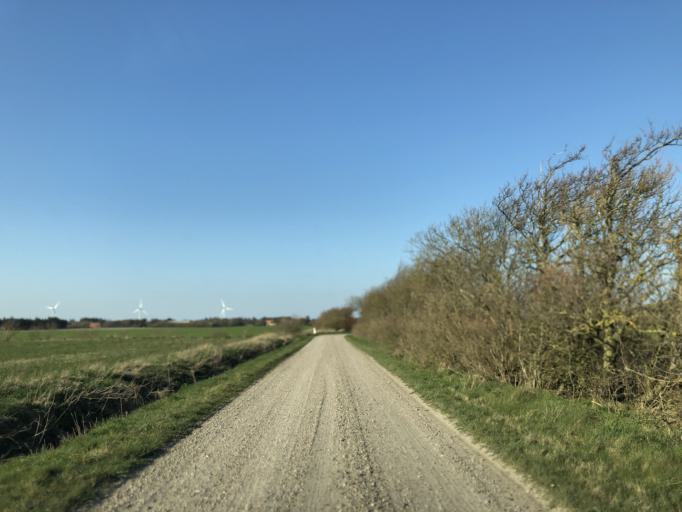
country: DK
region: Central Jutland
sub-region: Holstebro Kommune
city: Ulfborg
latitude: 56.3560
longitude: 8.2491
